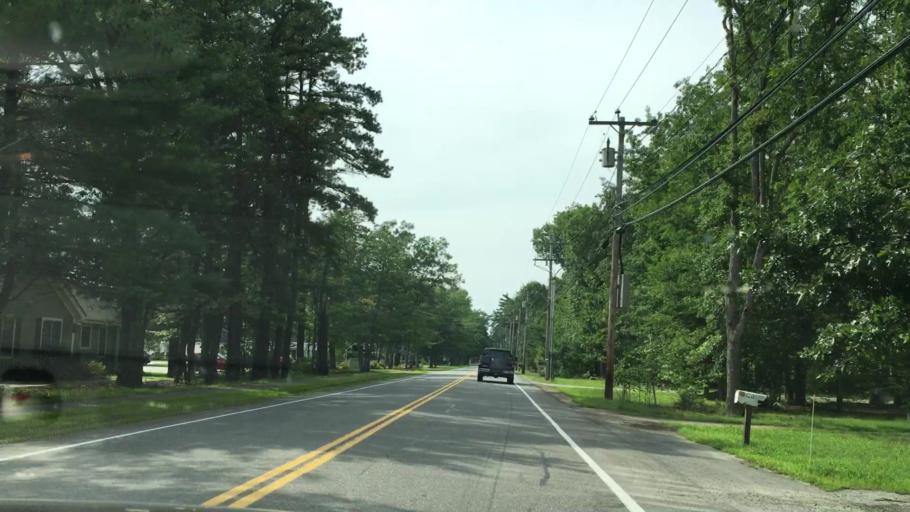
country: US
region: New Hampshire
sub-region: Merrimack County
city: East Concord
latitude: 43.2289
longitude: -71.5130
